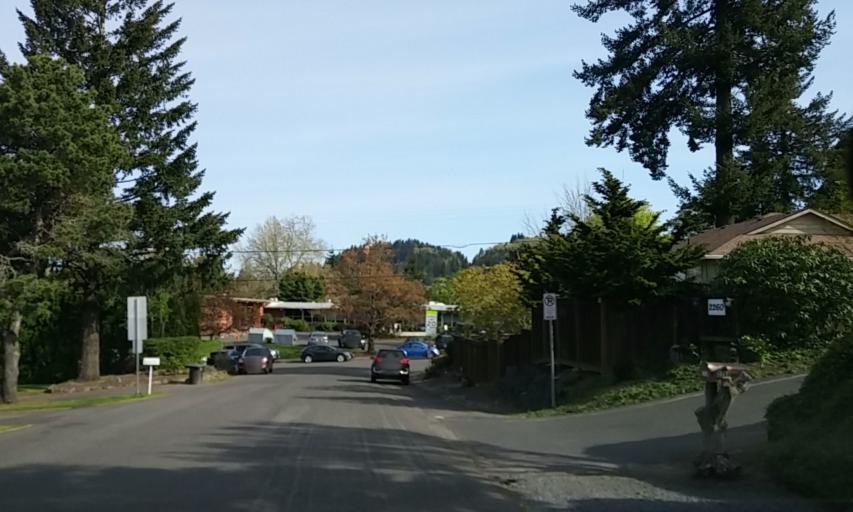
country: US
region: Oregon
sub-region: Washington County
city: West Slope
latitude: 45.5034
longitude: -122.7603
